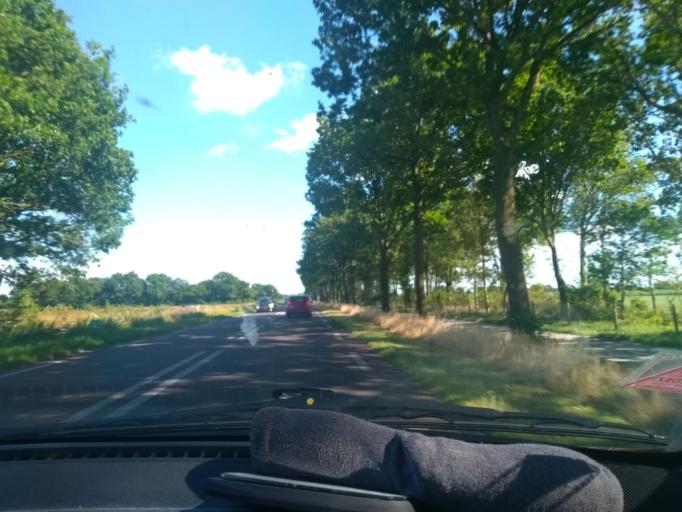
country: NL
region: Drenthe
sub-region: Gemeente Tynaarlo
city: Vries
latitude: 53.1157
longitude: 6.5130
